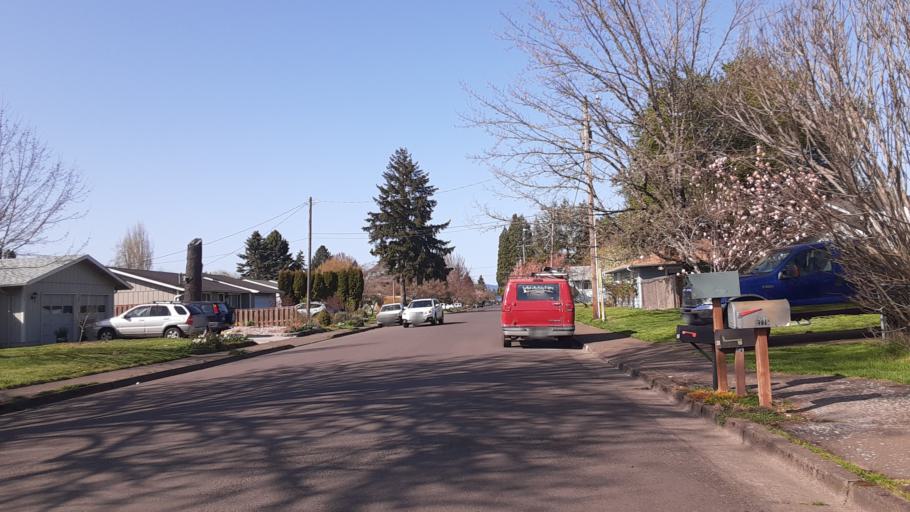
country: US
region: Oregon
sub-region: Benton County
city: Corvallis
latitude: 44.5390
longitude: -123.2602
